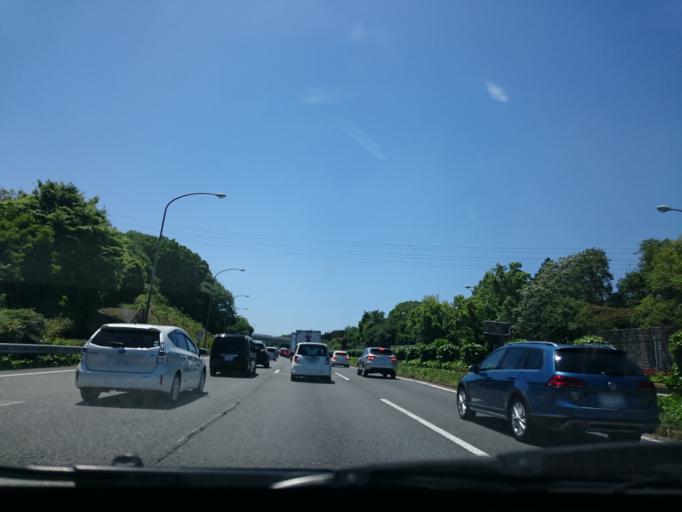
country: JP
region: Tokyo
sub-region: Machida-shi
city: Machida
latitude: 35.5118
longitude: 139.4874
